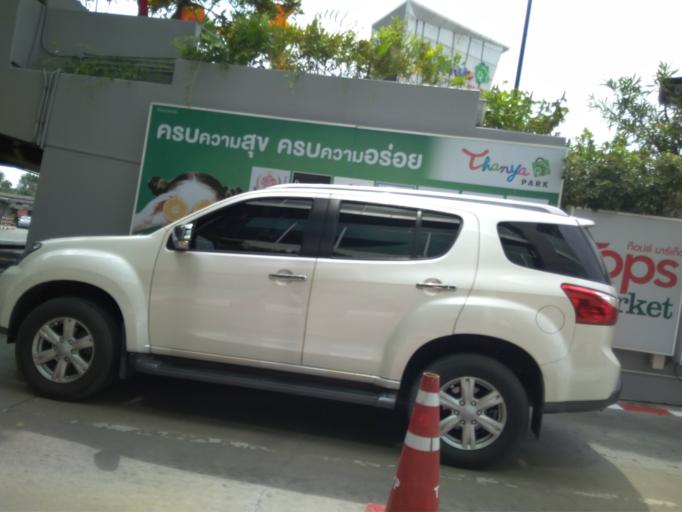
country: TH
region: Bangkok
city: Suan Luang
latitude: 13.7259
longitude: 100.6421
